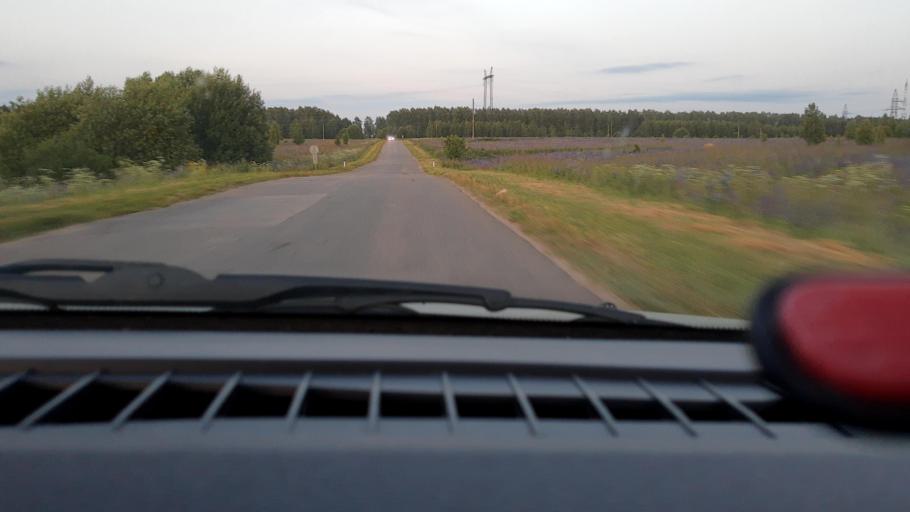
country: RU
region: Nizjnij Novgorod
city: Surovatikha
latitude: 55.8474
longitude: 43.9646
